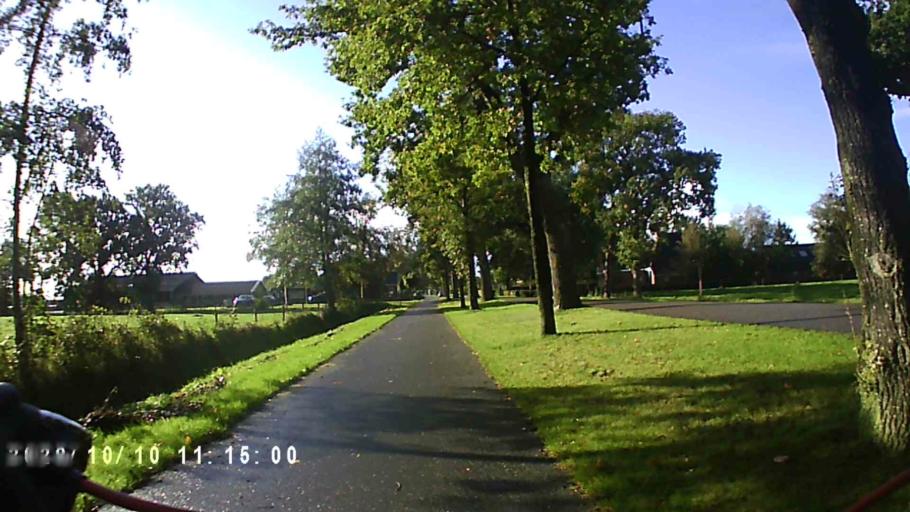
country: NL
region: Friesland
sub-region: Gemeente Smallingerland
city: Drachtstercompagnie
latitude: 53.1041
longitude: 6.2022
